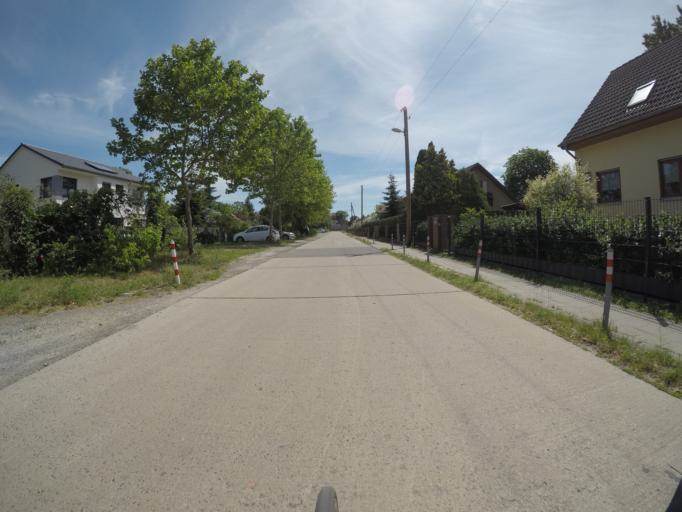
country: DE
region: Berlin
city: Mahlsdorf
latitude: 52.4951
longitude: 13.6074
